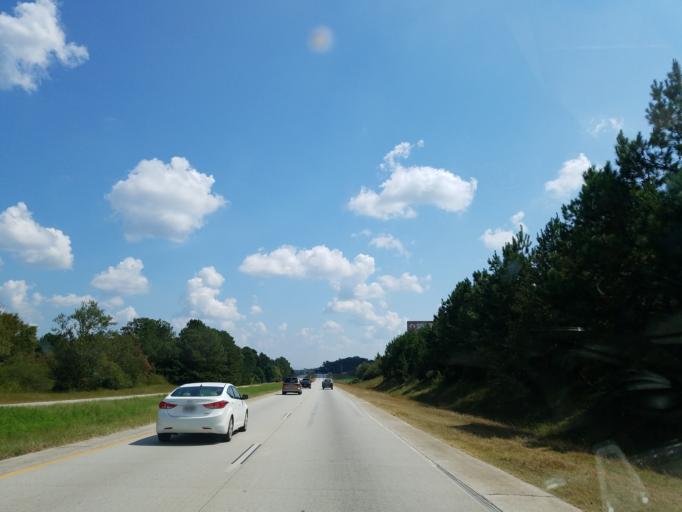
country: US
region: Georgia
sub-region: Barrow County
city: Winder
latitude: 33.9498
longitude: -83.7609
